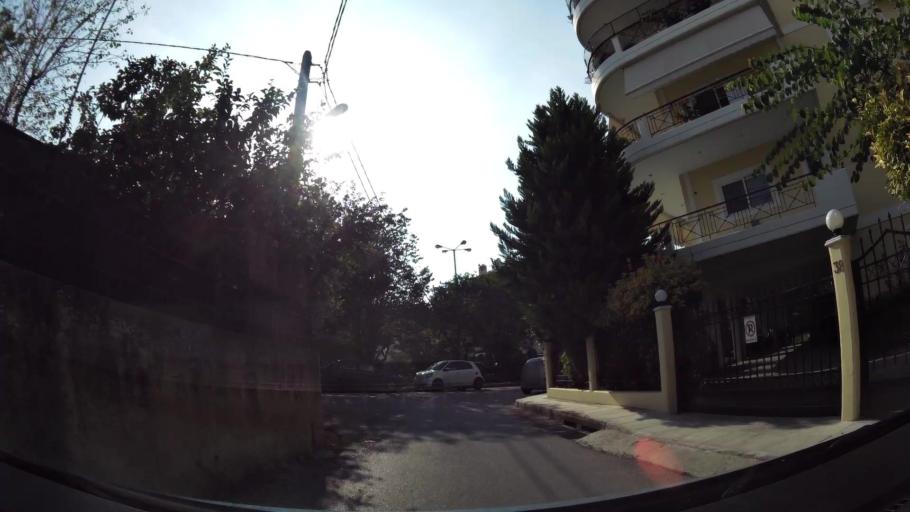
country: GR
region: Attica
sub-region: Nomarchia Athinas
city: Cholargos
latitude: 37.9984
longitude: 23.8108
